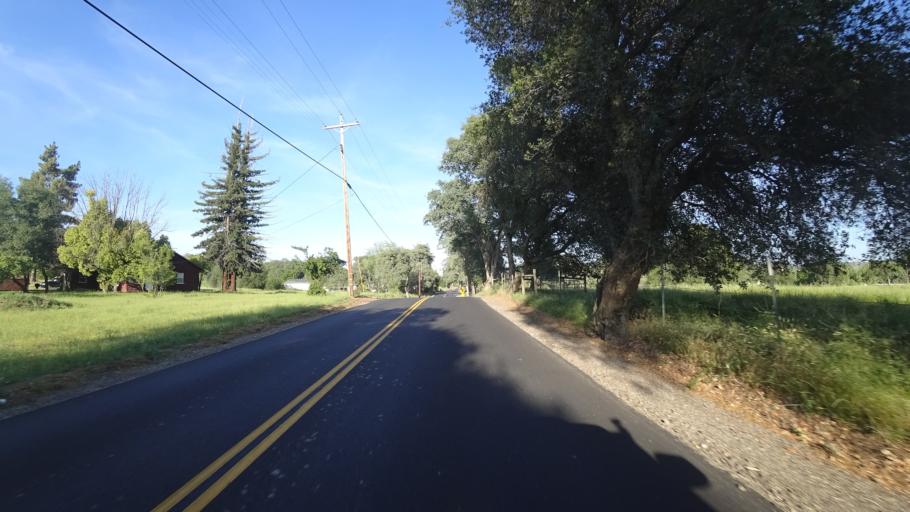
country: US
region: California
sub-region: Placer County
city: Lincoln
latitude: 38.9123
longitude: -121.2210
